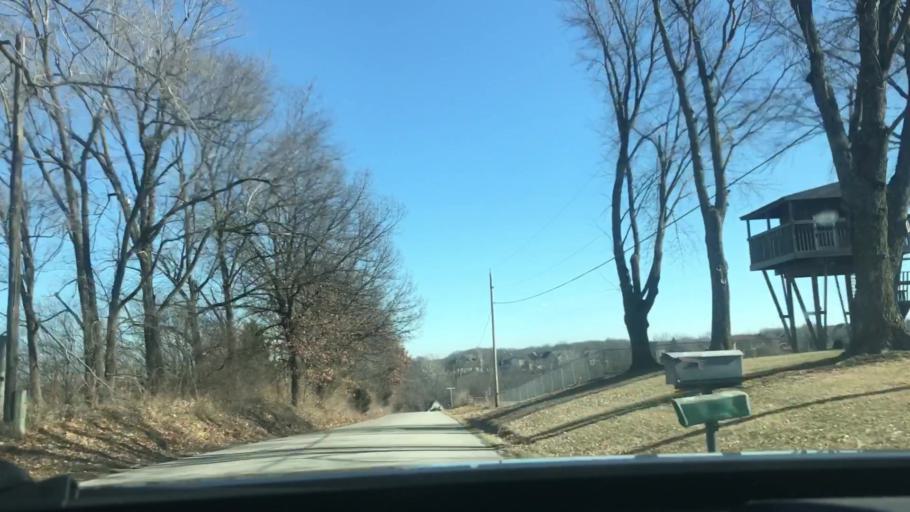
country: US
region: Kansas
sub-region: Leavenworth County
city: Leavenworth
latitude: 39.2813
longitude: -94.9535
